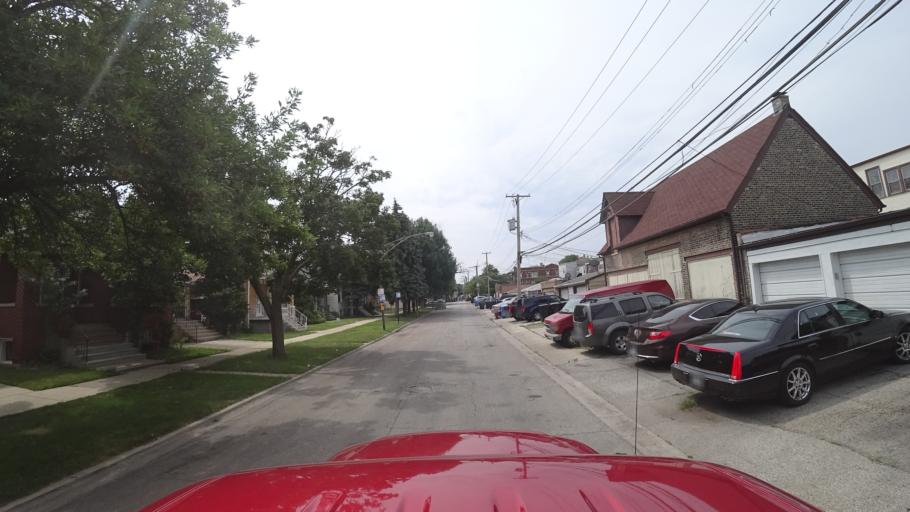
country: US
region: Illinois
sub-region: Cook County
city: Chicago
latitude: 41.8316
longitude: -87.6838
